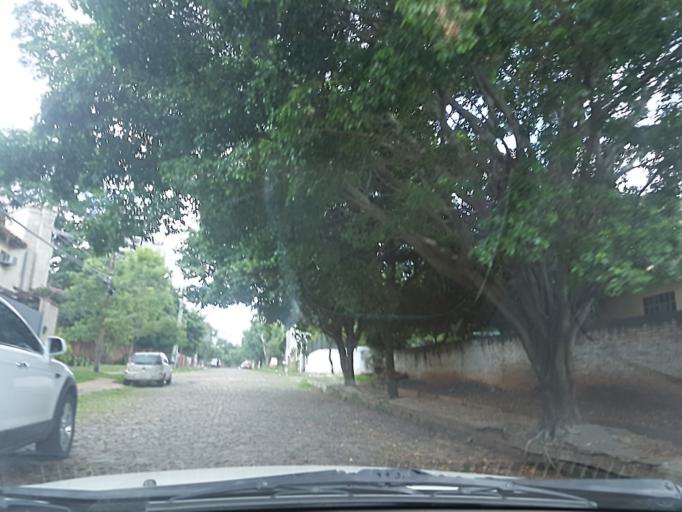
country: PY
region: Asuncion
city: Asuncion
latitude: -25.2669
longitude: -57.5726
